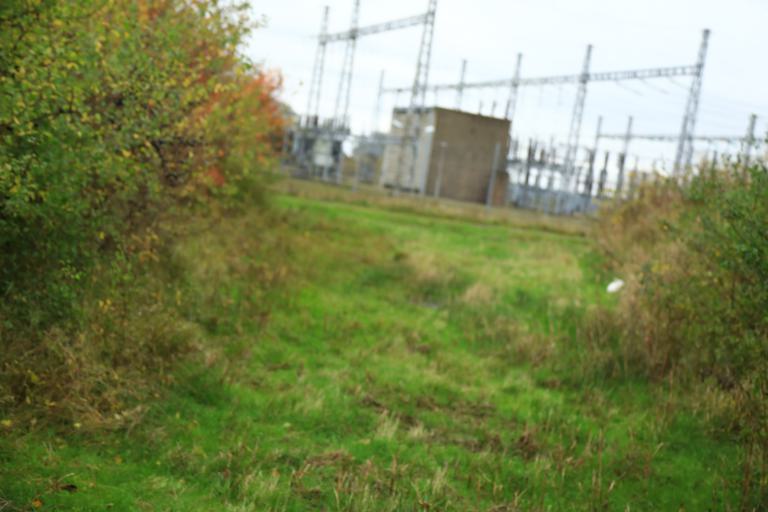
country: SE
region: Halland
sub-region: Varbergs Kommun
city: Varberg
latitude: 57.1273
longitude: 12.3010
